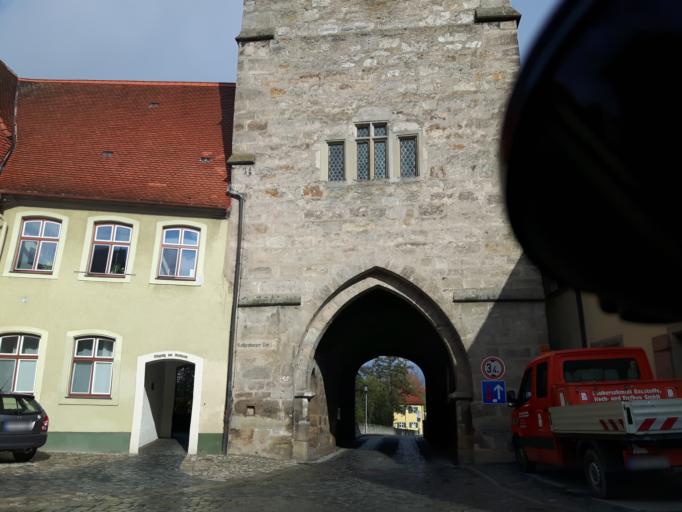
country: DE
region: Bavaria
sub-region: Regierungsbezirk Mittelfranken
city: Dinkelsbuhl
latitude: 49.0716
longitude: 10.3186
